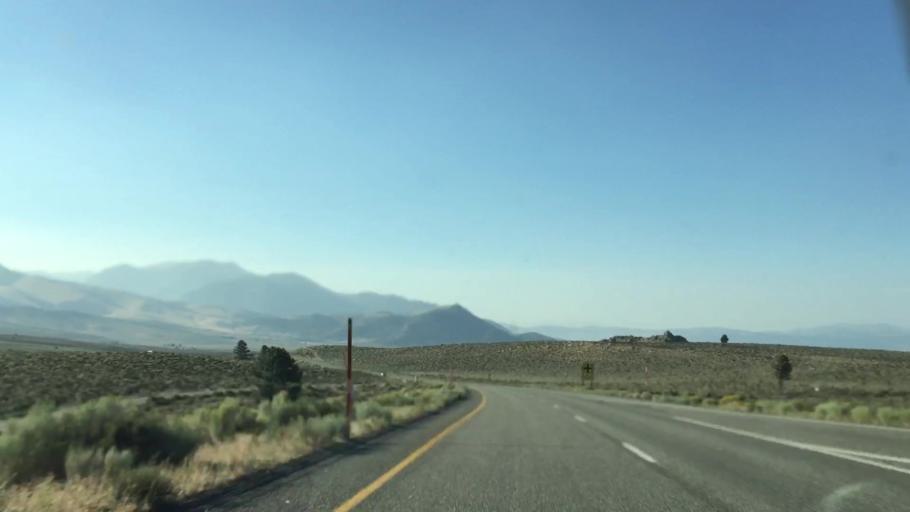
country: US
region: California
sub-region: Mono County
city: Mammoth Lakes
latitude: 37.8402
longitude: -119.0709
